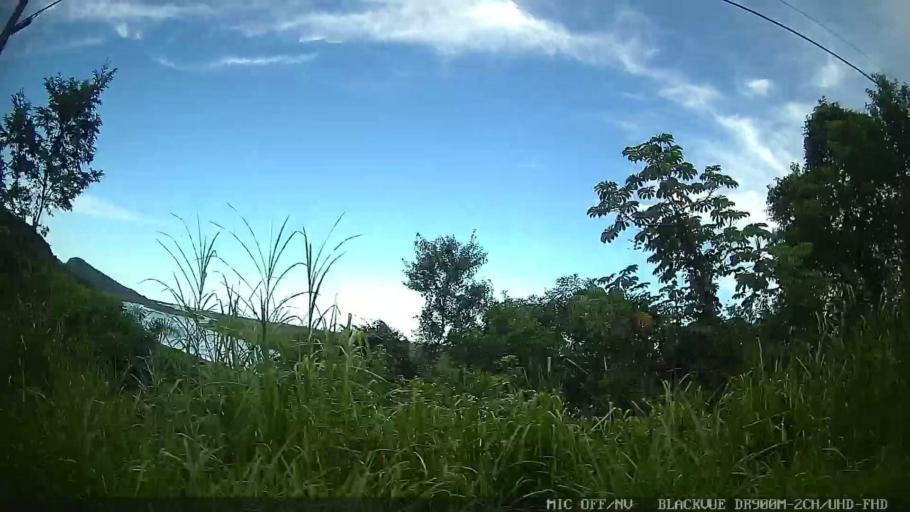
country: BR
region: Sao Paulo
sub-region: Iguape
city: Iguape
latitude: -24.7041
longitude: -47.5461
